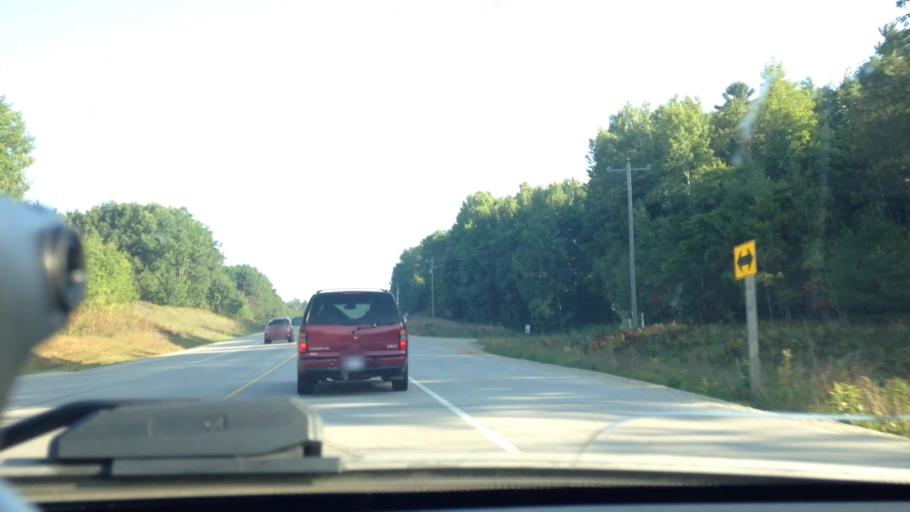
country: US
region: Wisconsin
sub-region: Marinette County
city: Peshtigo
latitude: 45.1648
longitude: -87.9964
